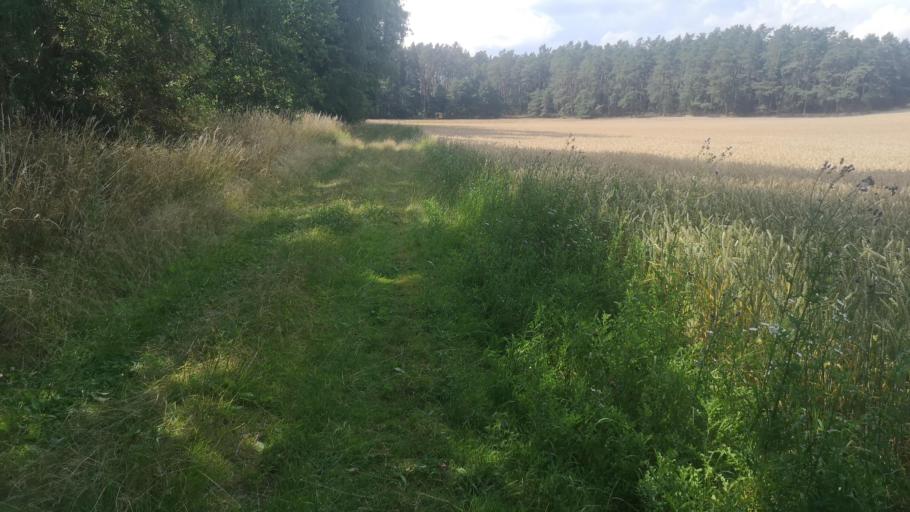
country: DE
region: Lower Saxony
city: Dahlem
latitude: 53.2197
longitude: 10.7476
